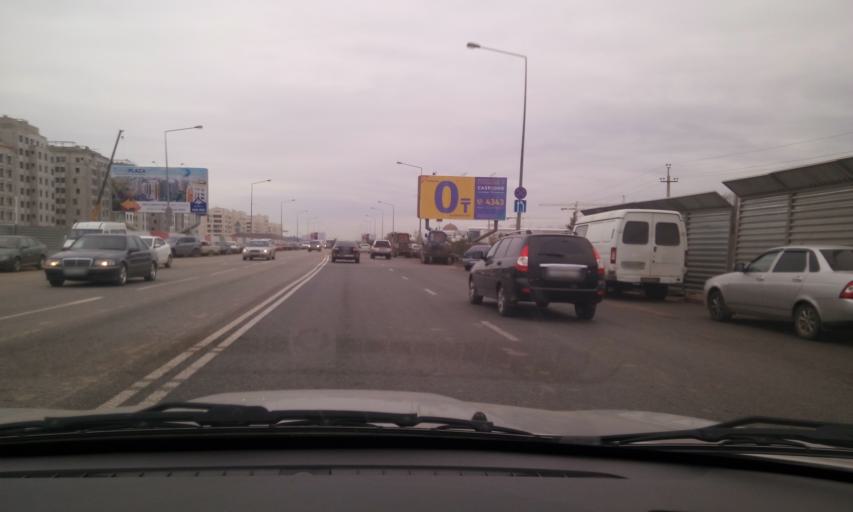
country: KZ
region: Astana Qalasy
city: Astana
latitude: 51.0984
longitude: 71.4058
